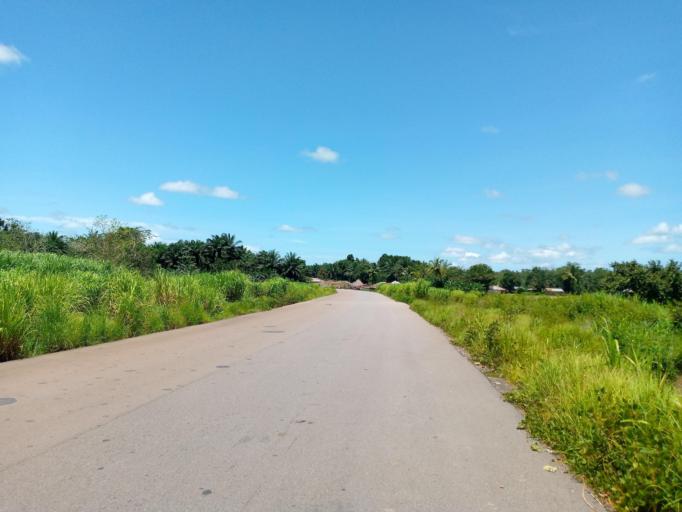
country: SL
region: Northern Province
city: Makeni
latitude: 9.0663
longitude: -12.1765
